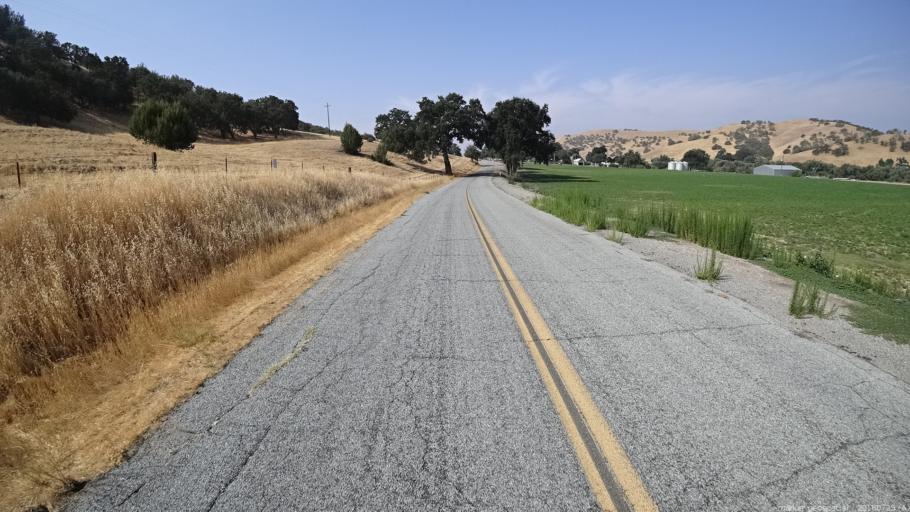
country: US
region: California
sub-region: San Luis Obispo County
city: San Miguel
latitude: 35.8110
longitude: -120.6686
